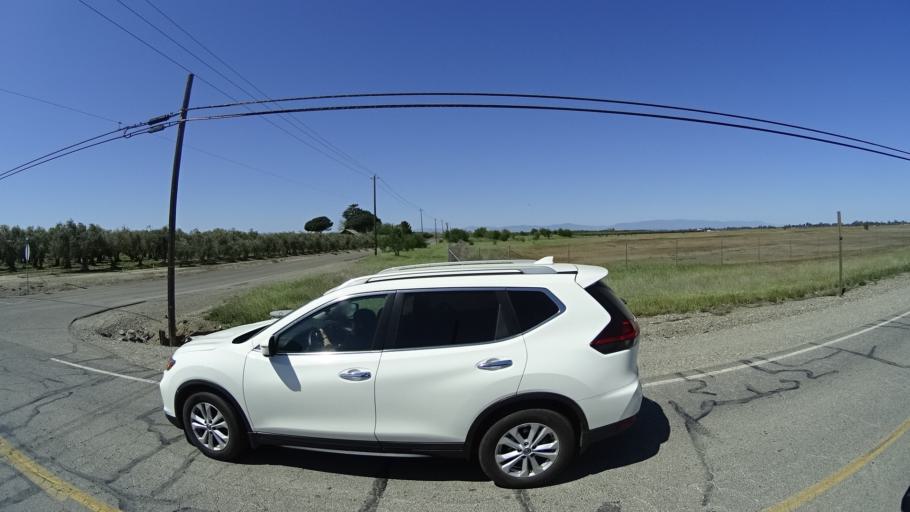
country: US
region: California
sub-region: Glenn County
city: Orland
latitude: 39.7108
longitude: -122.1410
